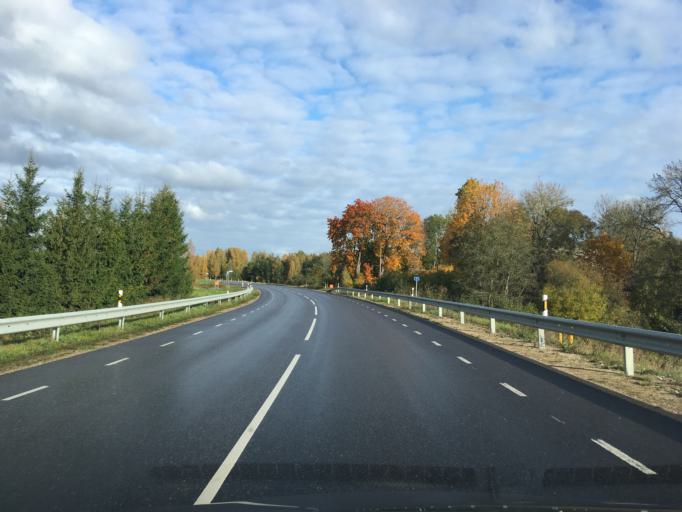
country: EE
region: Harju
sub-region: Raasiku vald
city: Raasiku
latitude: 59.1931
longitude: 25.1853
